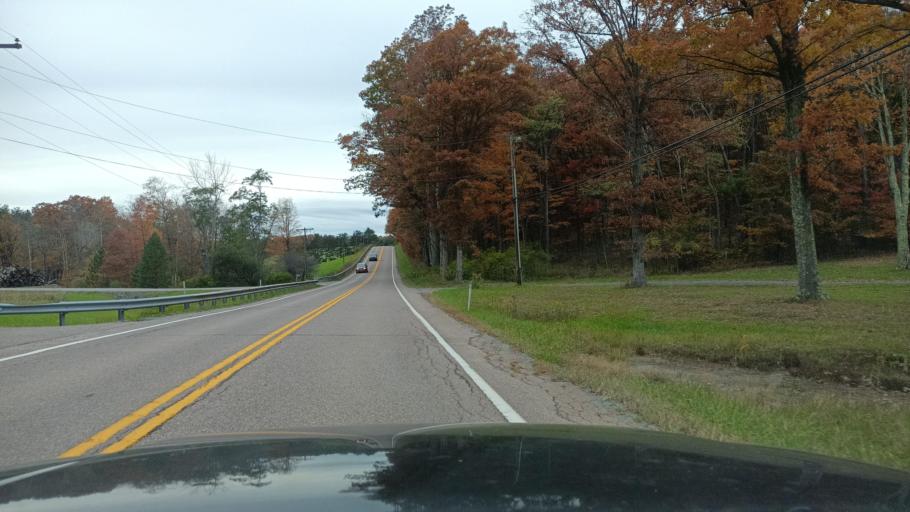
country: US
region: Maryland
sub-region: Garrett County
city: Oakland
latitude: 39.2989
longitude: -79.4390
